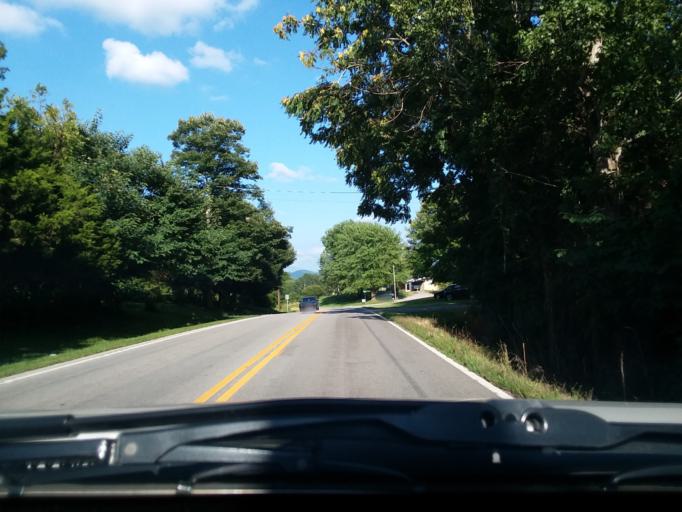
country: US
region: Tennessee
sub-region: Clay County
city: Celina
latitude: 36.5929
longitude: -85.5942
